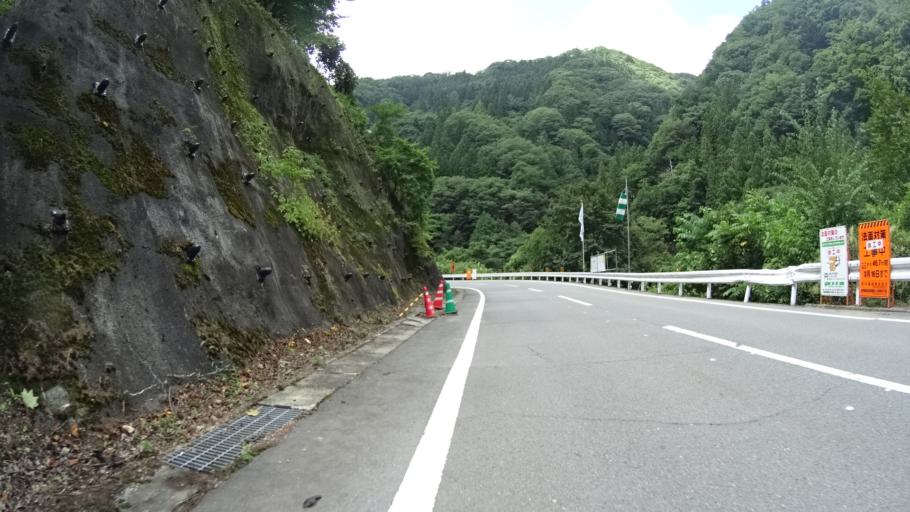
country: JP
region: Gunma
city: Tomioka
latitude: 36.0768
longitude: 138.7081
